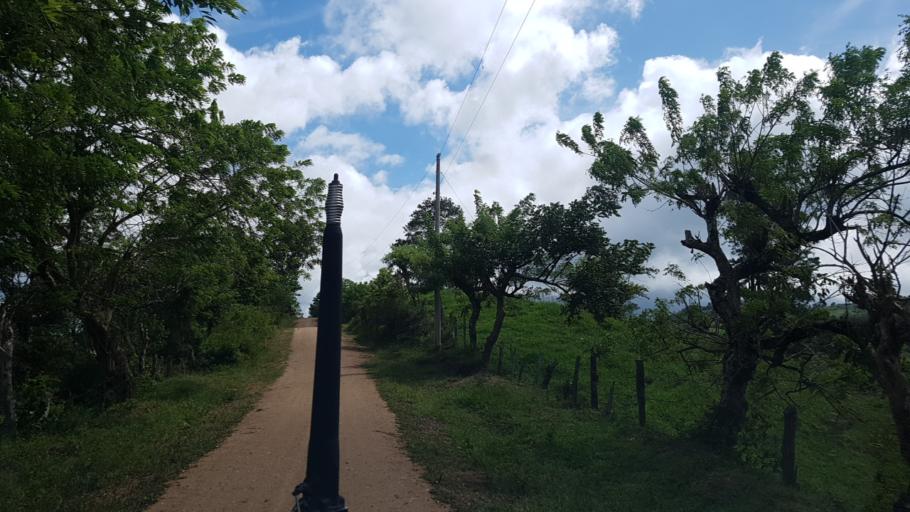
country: NI
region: Nueva Segovia
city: Ciudad Antigua
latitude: 13.6528
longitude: -86.2442
